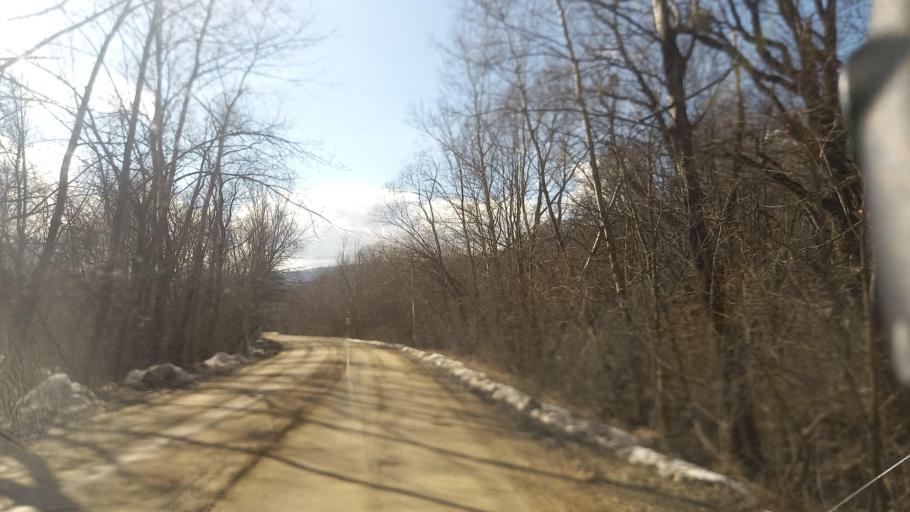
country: RU
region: Krasnodarskiy
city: Smolenskaya
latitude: 44.6656
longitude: 38.7390
